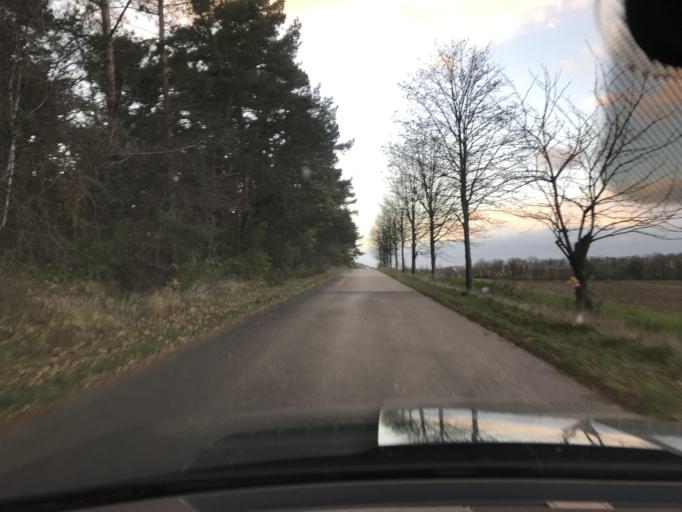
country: DE
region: Saxony-Anhalt
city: Langenstein
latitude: 51.8448
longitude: 11.0209
